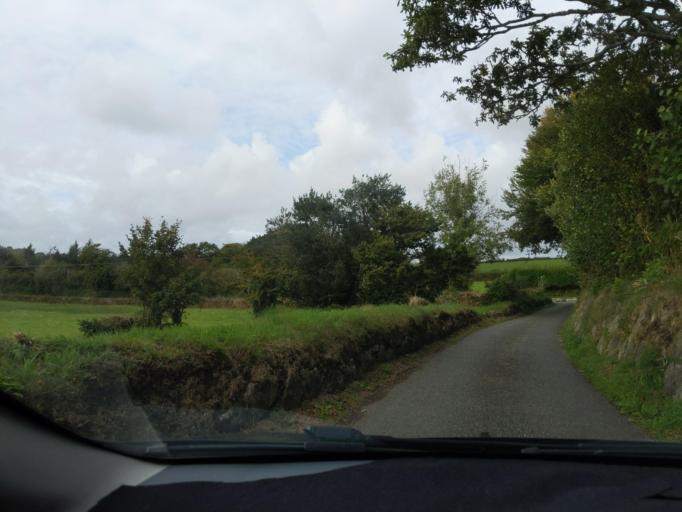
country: GB
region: England
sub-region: Cornwall
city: Lostwithiel
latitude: 50.4006
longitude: -4.6945
